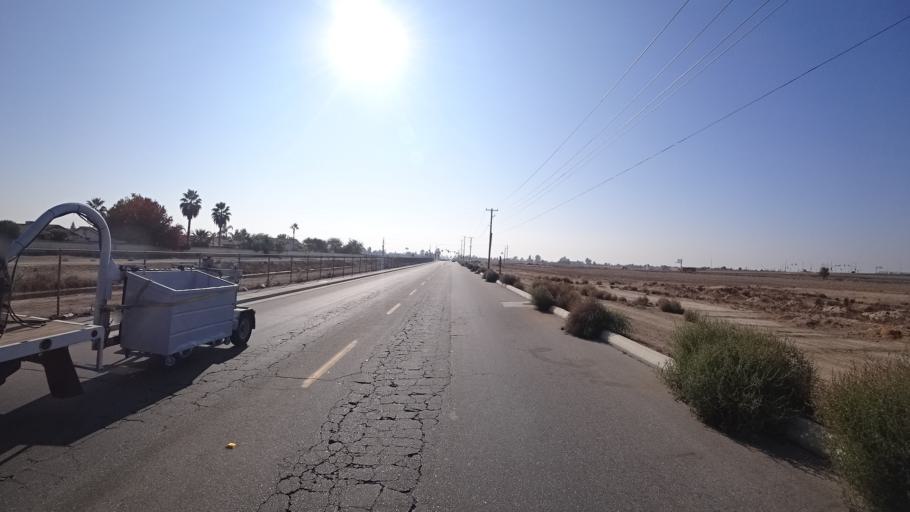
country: US
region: California
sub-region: Kern County
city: Greenfield
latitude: 35.2835
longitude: -119.0213
